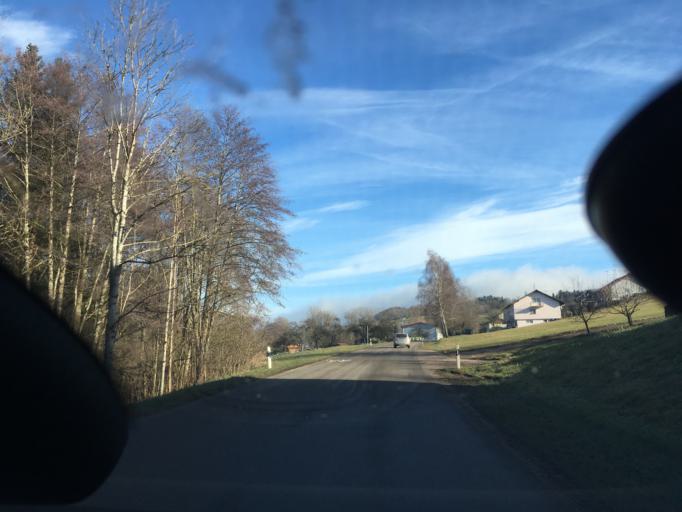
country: DE
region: Baden-Wuerttemberg
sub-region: Freiburg Region
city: Gorwihl
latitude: 47.6442
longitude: 8.1278
